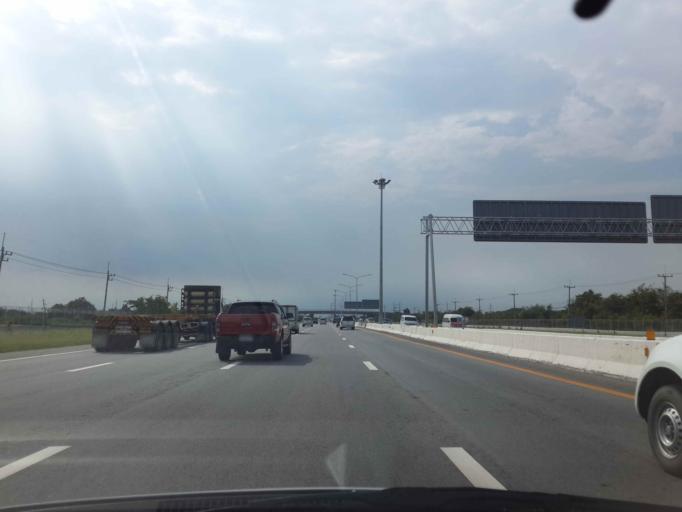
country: TH
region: Chachoengsao
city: Bang Pakong
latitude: 13.6063
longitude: 100.9430
